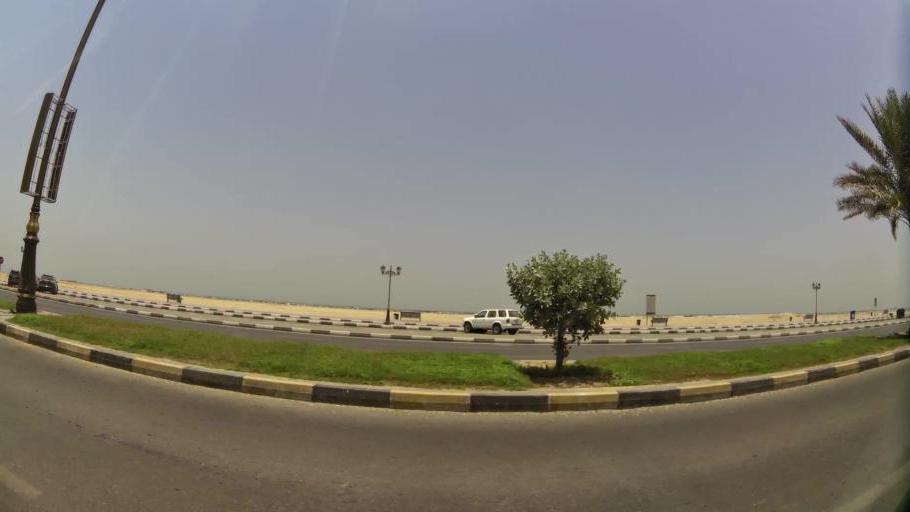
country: AE
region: Ajman
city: Ajman
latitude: 25.4128
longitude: 55.4361
